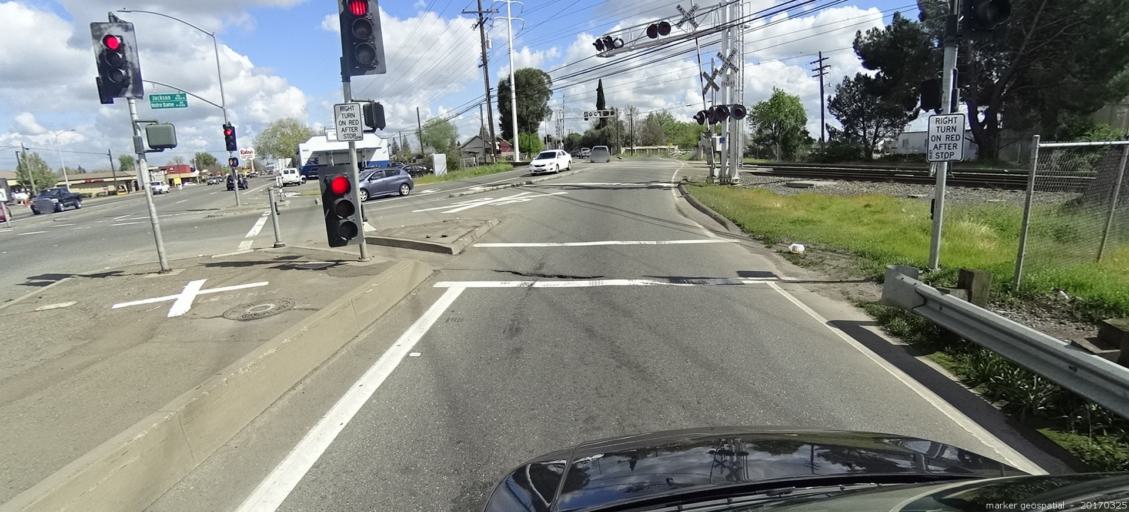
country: US
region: California
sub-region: Sacramento County
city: Rosemont
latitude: 38.5469
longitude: -121.3993
